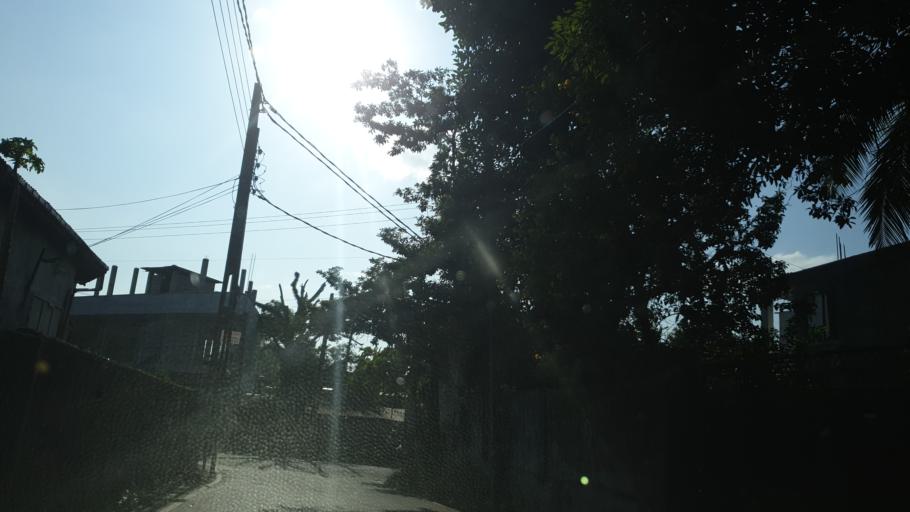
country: LK
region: Western
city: Battaramulla South
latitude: 6.8857
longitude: 79.9416
